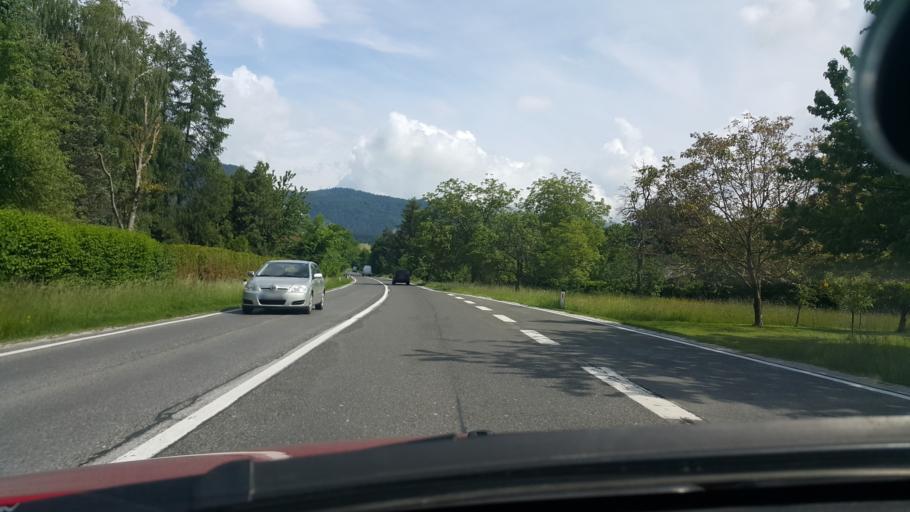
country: SI
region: Trzic
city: Bistrica pri Trzicu
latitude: 46.3284
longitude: 14.2814
